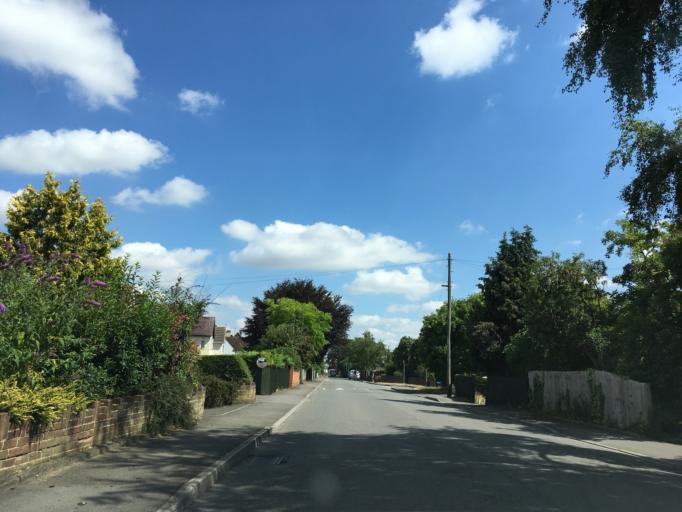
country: GB
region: England
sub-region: Gloucestershire
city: Barnwood
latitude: 51.8766
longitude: -2.2183
